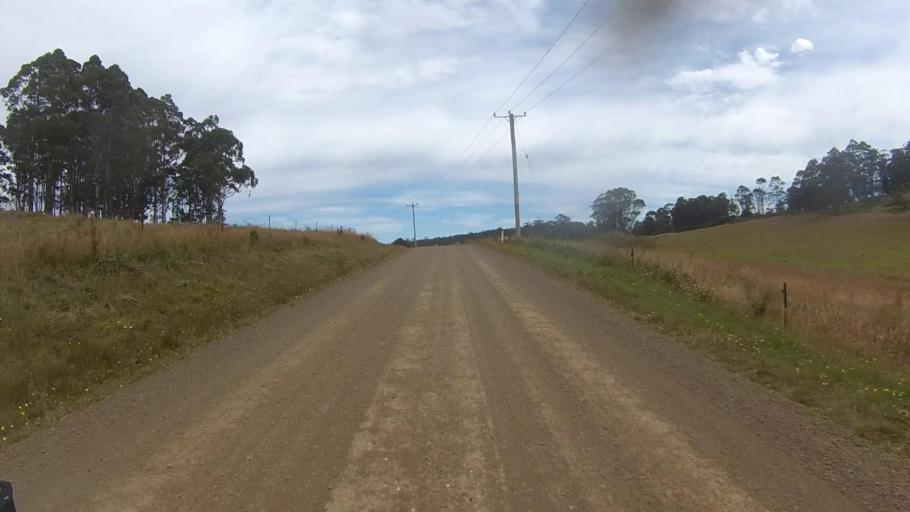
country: AU
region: Tasmania
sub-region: Sorell
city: Sorell
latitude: -42.7231
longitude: 147.7516
